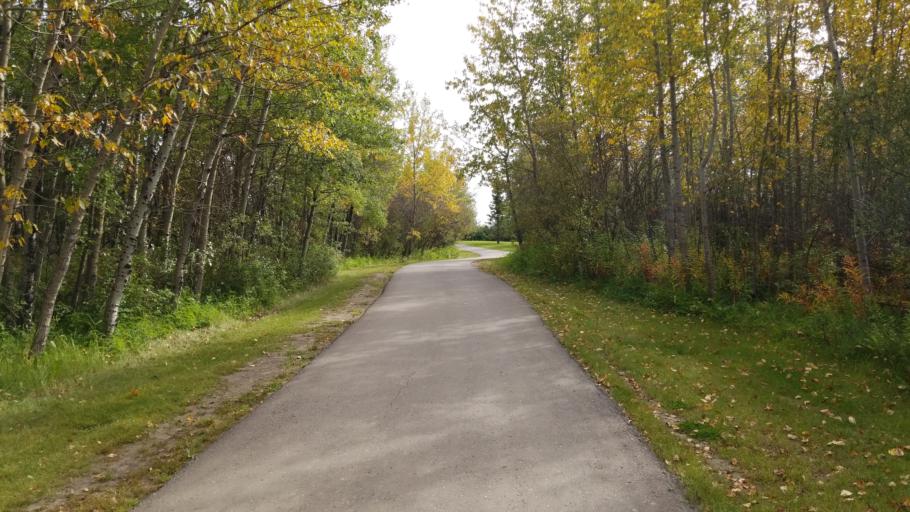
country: CA
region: Saskatchewan
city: Lloydminster
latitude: 53.2610
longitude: -110.0428
